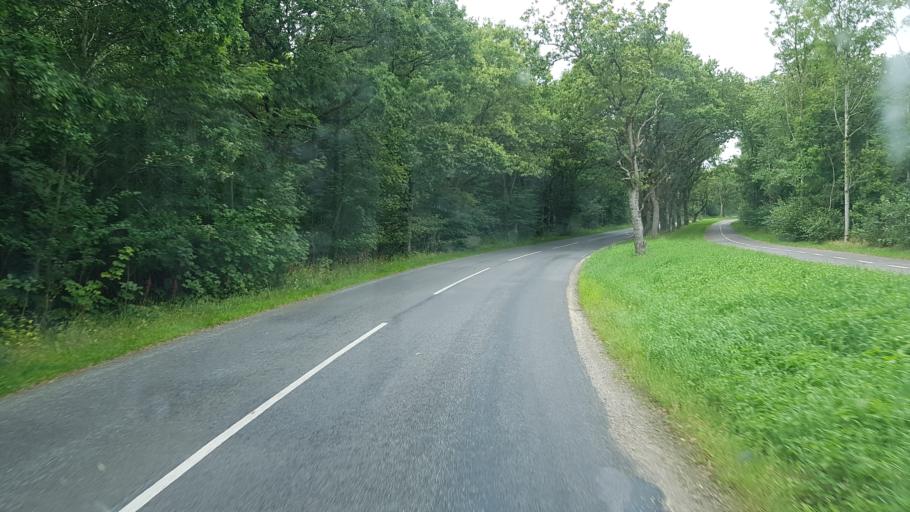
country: DK
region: South Denmark
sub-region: Varde Kommune
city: Olgod
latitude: 55.7051
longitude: 8.6406
